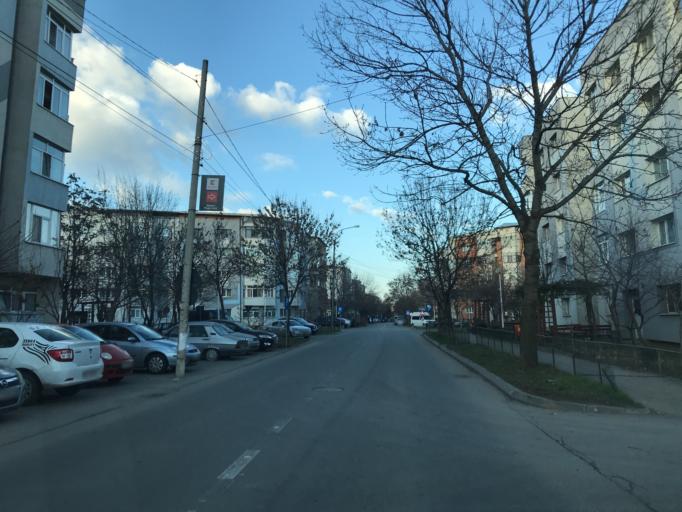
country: RO
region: Olt
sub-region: Municipiul Slatina
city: Slatina
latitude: 44.4169
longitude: 24.3804
